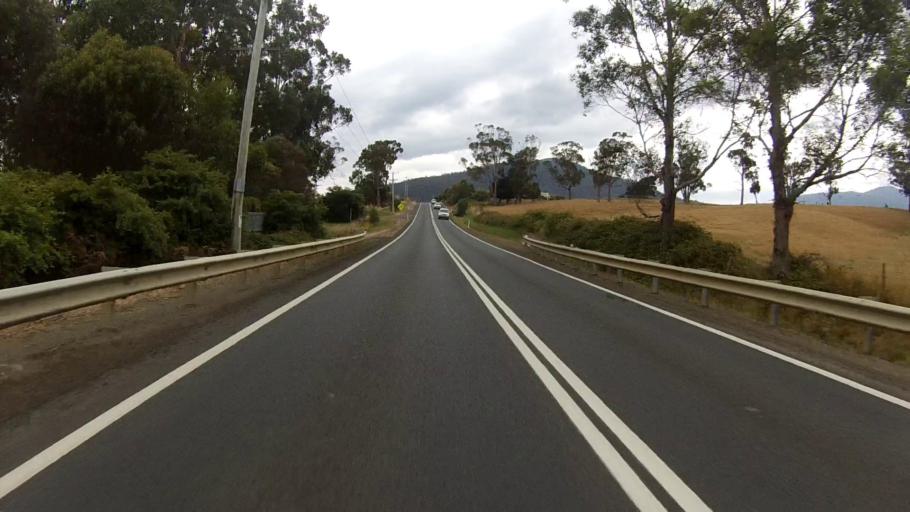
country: AU
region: Tasmania
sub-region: Huon Valley
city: Franklin
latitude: -43.0758
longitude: 147.0341
